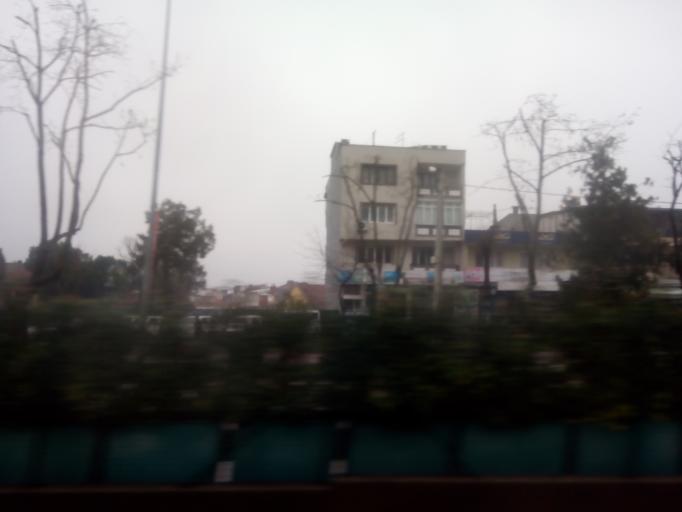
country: TR
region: Bursa
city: Yildirim
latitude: 40.2037
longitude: 29.0328
